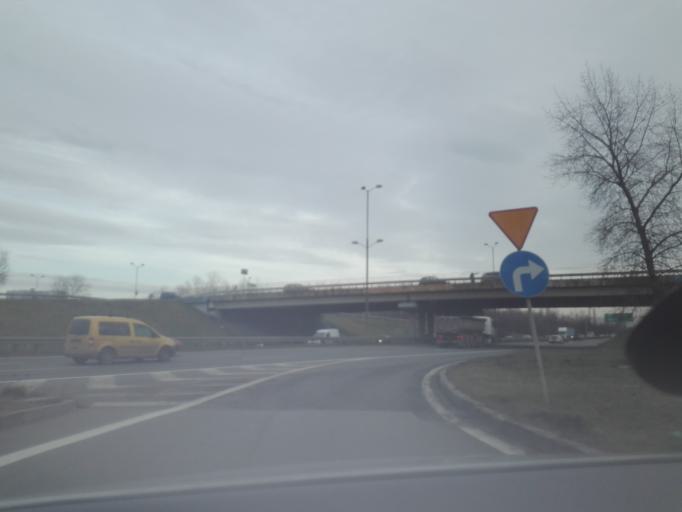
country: PL
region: Silesian Voivodeship
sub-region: Chorzow
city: Chorzow
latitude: 50.2718
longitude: 18.9739
